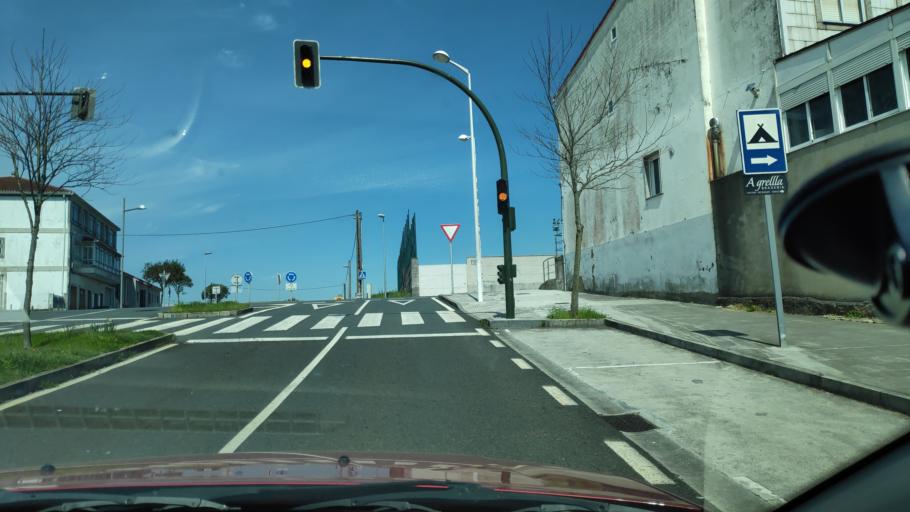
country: ES
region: Galicia
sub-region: Provincia da Coruna
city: Santiago de Compostela
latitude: 42.8909
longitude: -8.5265
